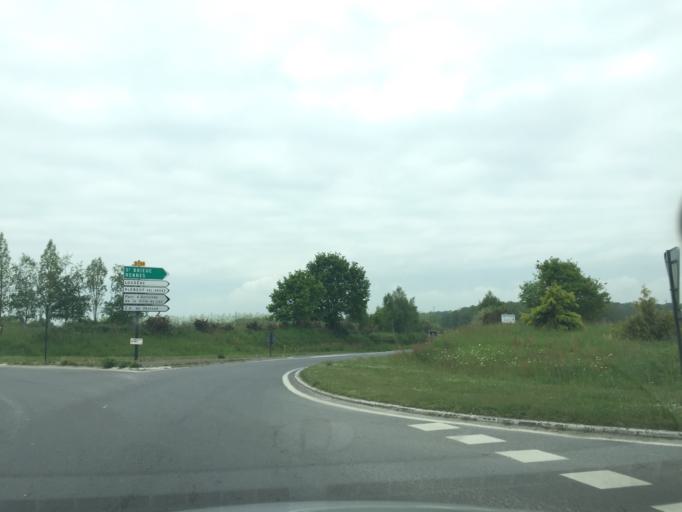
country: FR
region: Brittany
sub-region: Departement des Cotes-d'Armor
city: Lamballe
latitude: 48.4800
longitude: -2.4990
